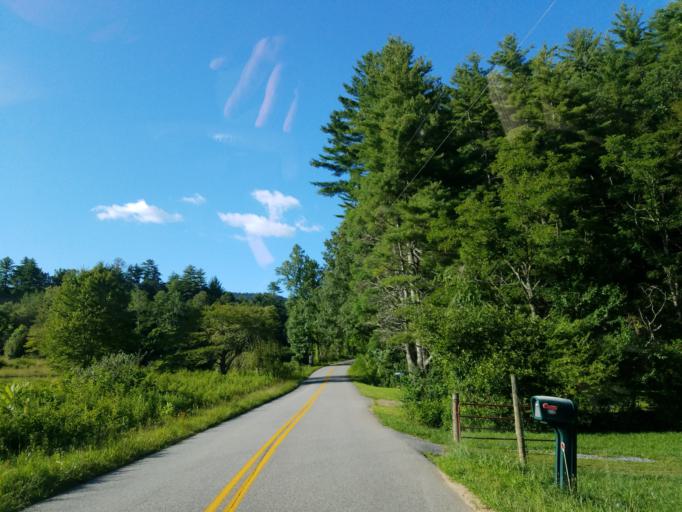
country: US
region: Georgia
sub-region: Union County
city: Blairsville
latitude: 34.7548
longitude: -84.1151
